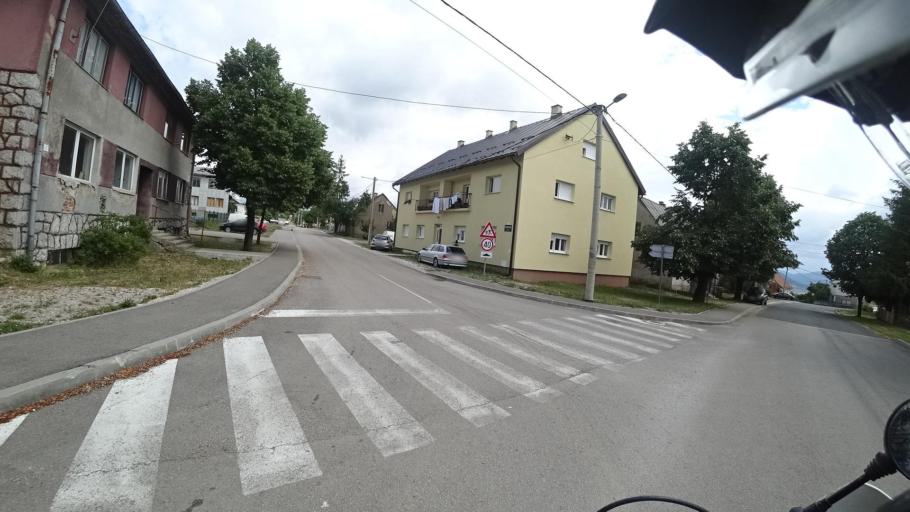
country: HR
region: Zadarska
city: Gracac
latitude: 44.5314
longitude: 15.7668
